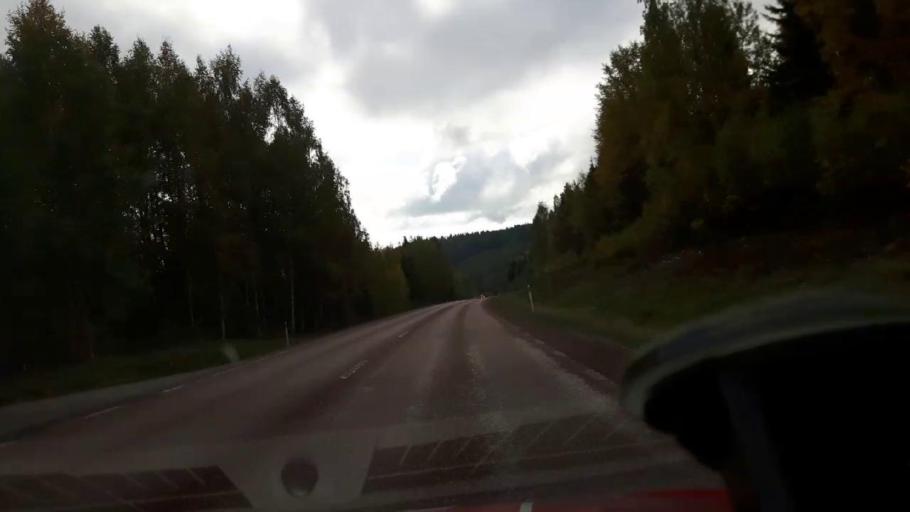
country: SE
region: Gaevleborg
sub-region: Bollnas Kommun
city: Arbra
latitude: 61.6023
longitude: 16.2967
